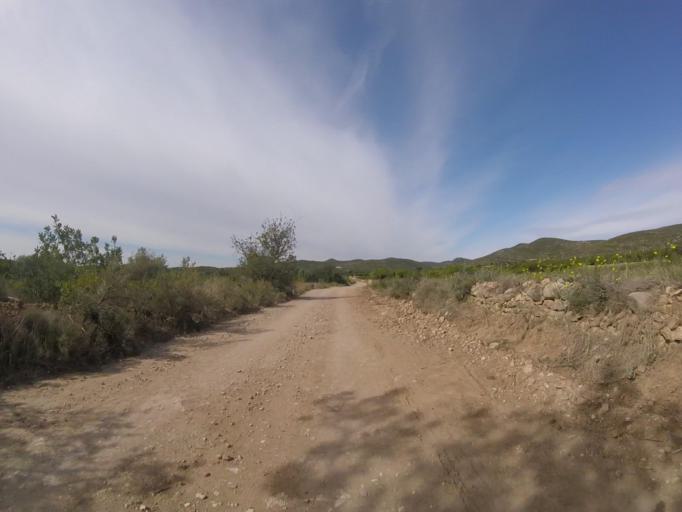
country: ES
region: Valencia
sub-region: Provincia de Castello
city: Torreblanca
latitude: 40.1993
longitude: 0.1649
